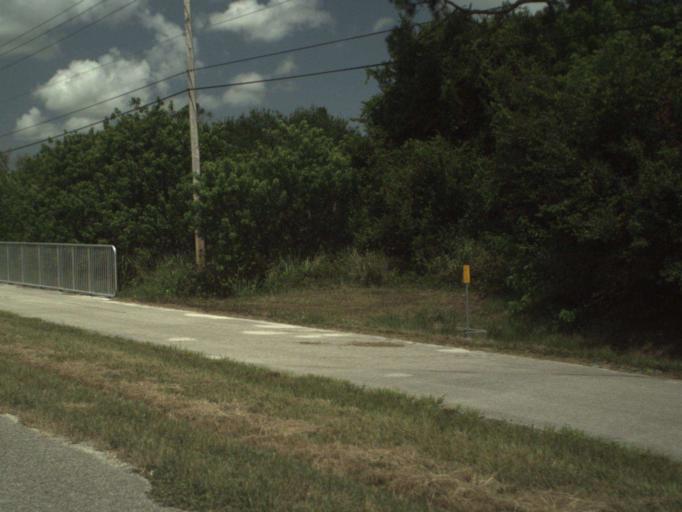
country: US
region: Florida
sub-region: Saint Lucie County
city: Fort Pierce South
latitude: 27.4051
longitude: -80.4356
